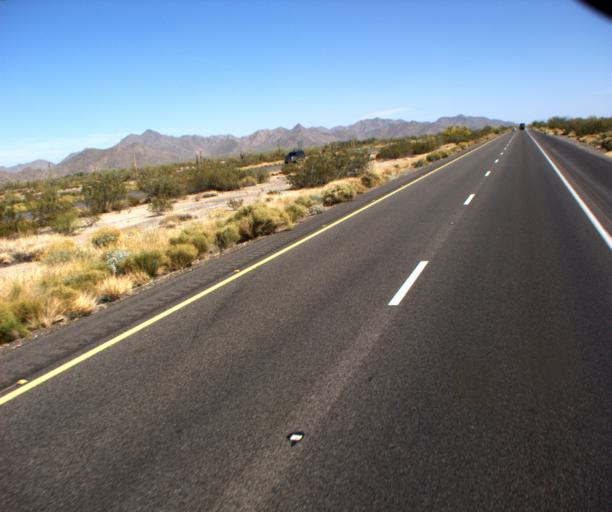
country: US
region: Arizona
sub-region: Maricopa County
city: Gila Bend
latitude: 32.8939
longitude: -112.4948
